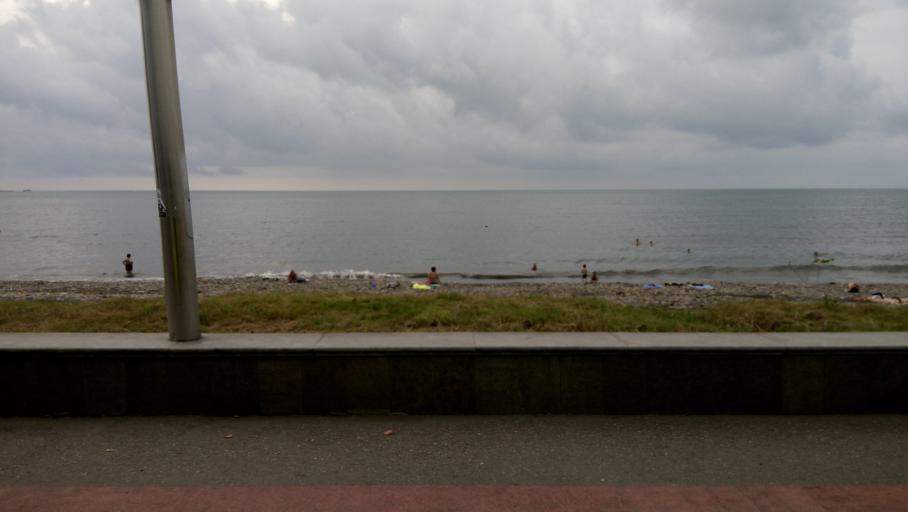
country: GE
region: Ajaria
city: Makhinjauri
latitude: 41.6523
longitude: 41.6700
